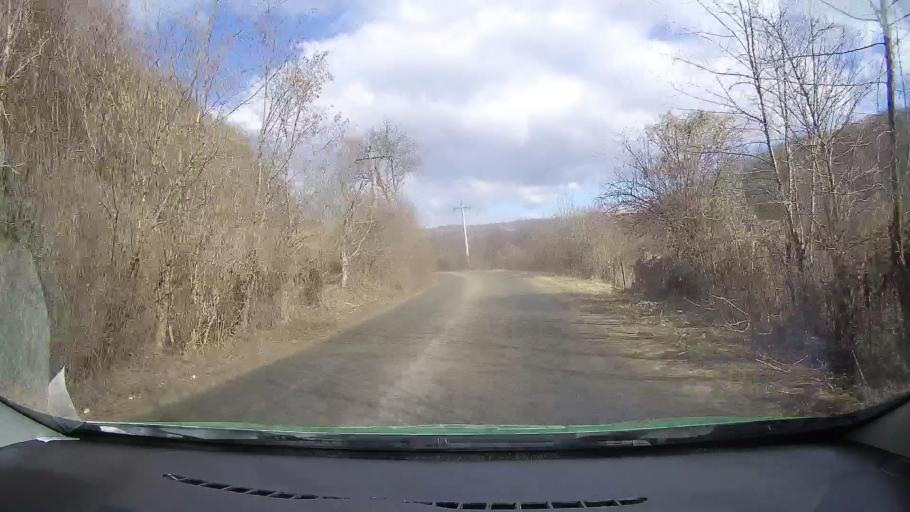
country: RO
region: Dambovita
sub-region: Comuna Motaeni
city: Motaeni
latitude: 45.1062
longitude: 25.4423
